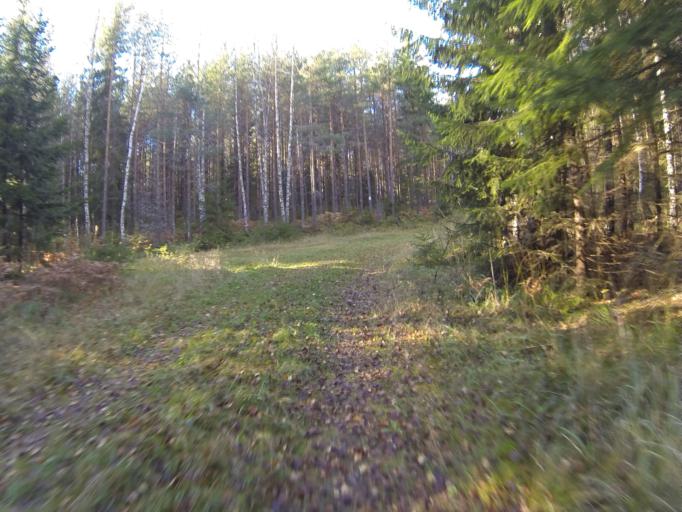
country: FI
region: Varsinais-Suomi
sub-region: Salo
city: Saerkisalo
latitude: 60.2238
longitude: 22.9604
